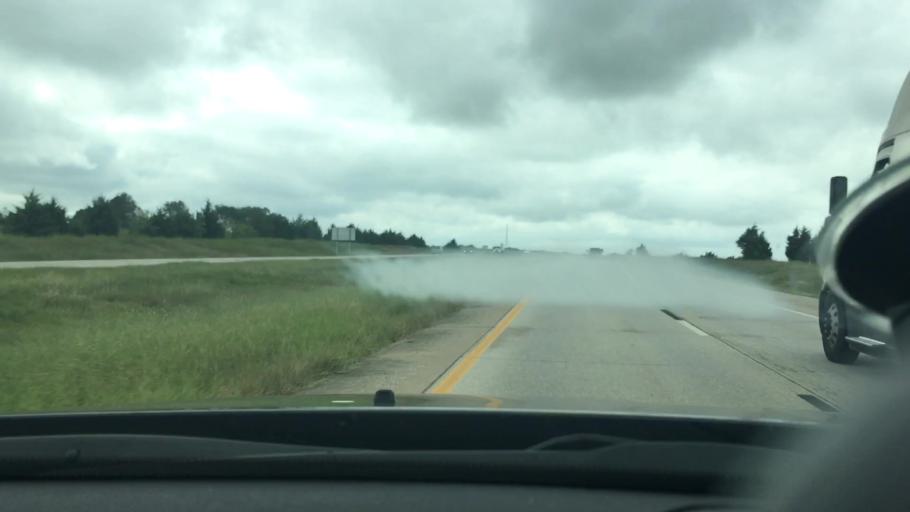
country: US
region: Oklahoma
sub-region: Bryan County
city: Durant
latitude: 34.1604
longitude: -96.2582
